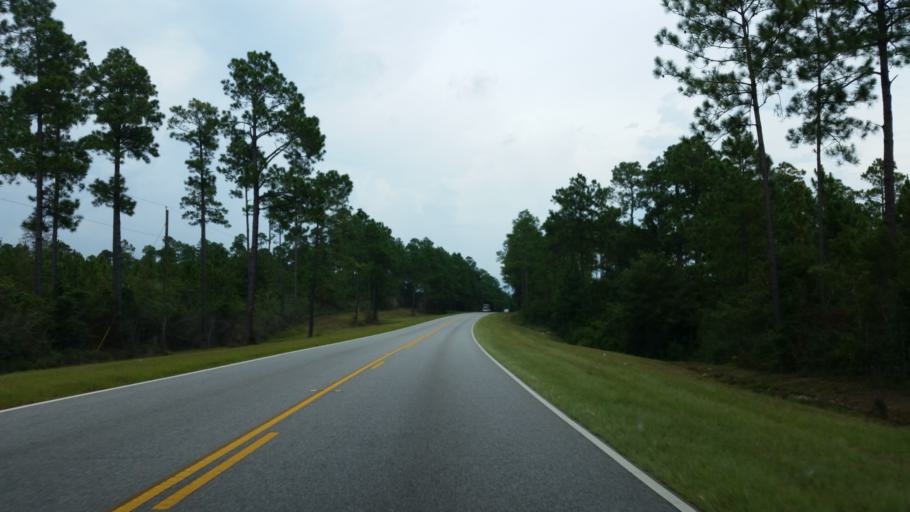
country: US
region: Florida
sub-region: Escambia County
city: Molino
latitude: 30.6612
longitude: -87.3010
